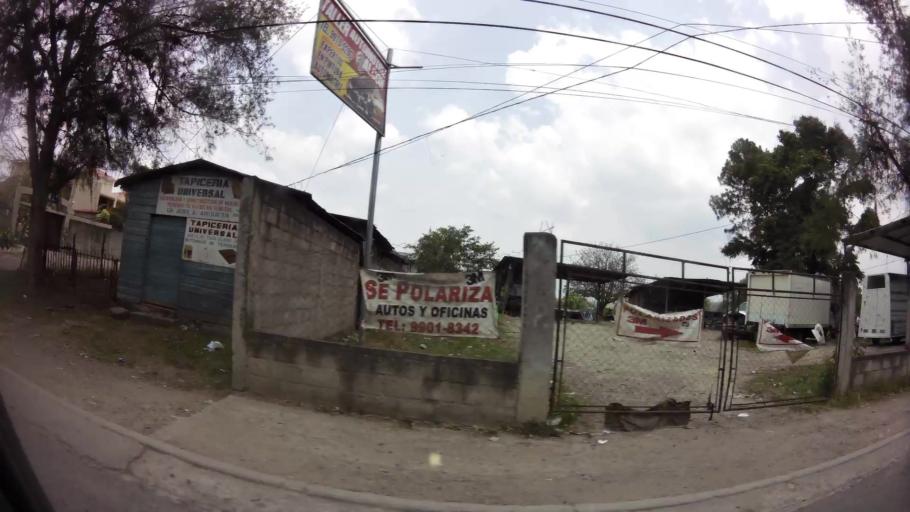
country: HN
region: Comayagua
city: Siguatepeque
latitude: 14.5929
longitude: -87.8320
